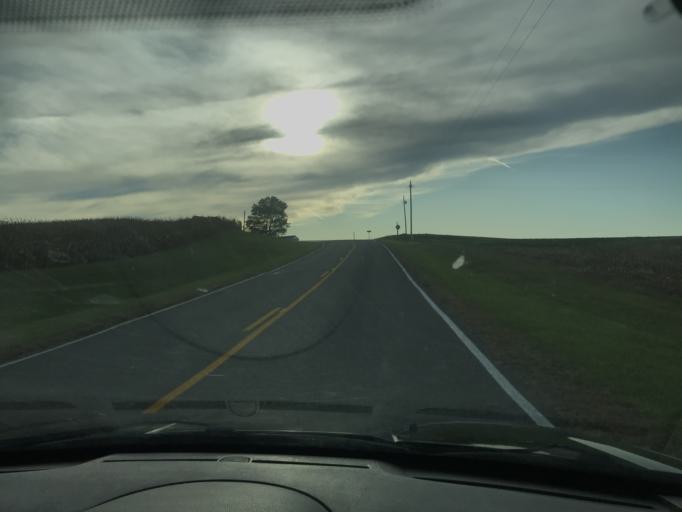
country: US
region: Ohio
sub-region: Logan County
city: West Liberty
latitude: 40.2112
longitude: -83.7004
